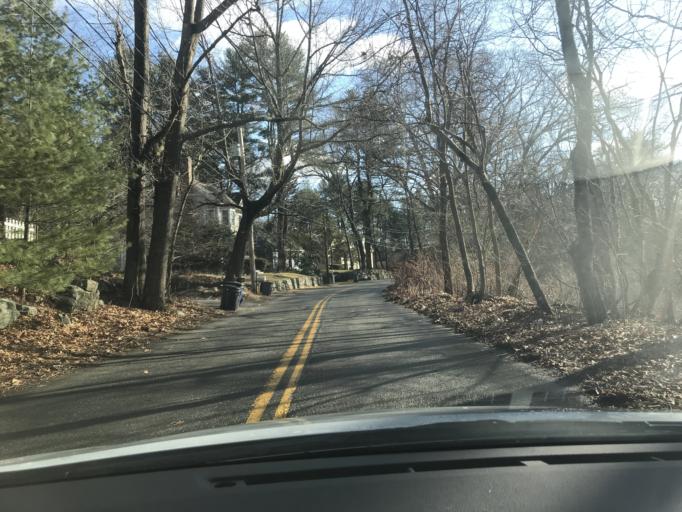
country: US
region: Massachusetts
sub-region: Middlesex County
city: Lexington
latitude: 42.4720
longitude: -71.2193
